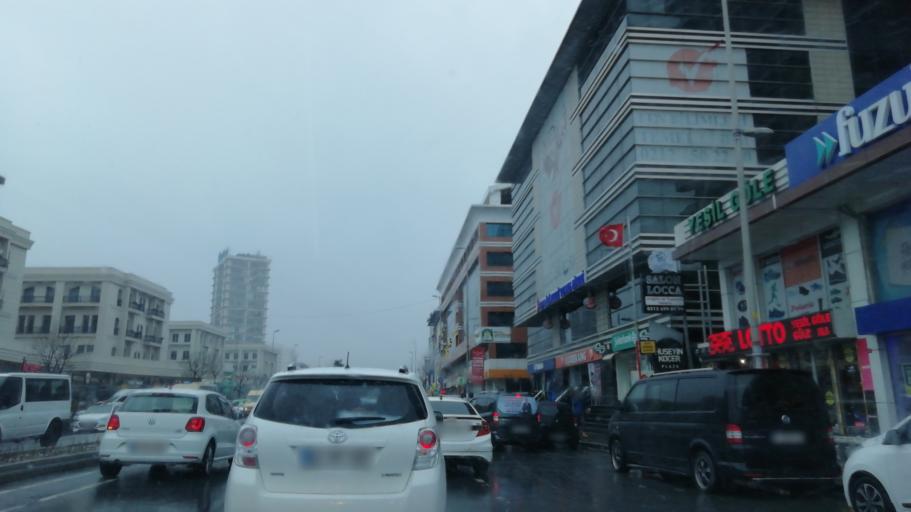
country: TR
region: Istanbul
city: Esenyurt
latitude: 41.0233
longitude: 28.6863
